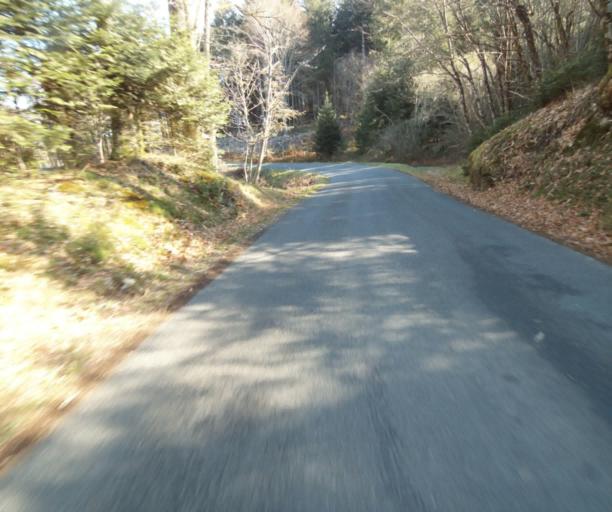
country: FR
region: Limousin
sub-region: Departement de la Correze
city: Correze
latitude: 45.2915
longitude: 1.8692
